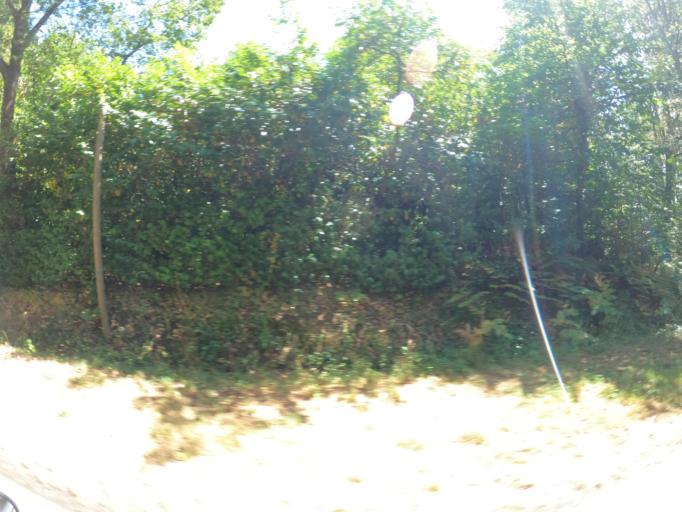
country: FR
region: Pays de la Loire
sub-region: Departement de Maine-et-Loire
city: Champigne
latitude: 47.6213
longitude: -0.5831
